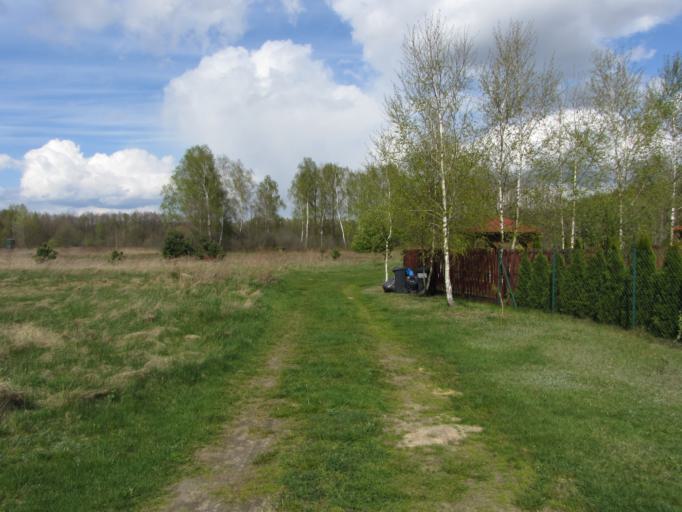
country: PL
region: Lubusz
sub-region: Powiat wschowski
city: Slawa
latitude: 51.8738
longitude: 15.9968
